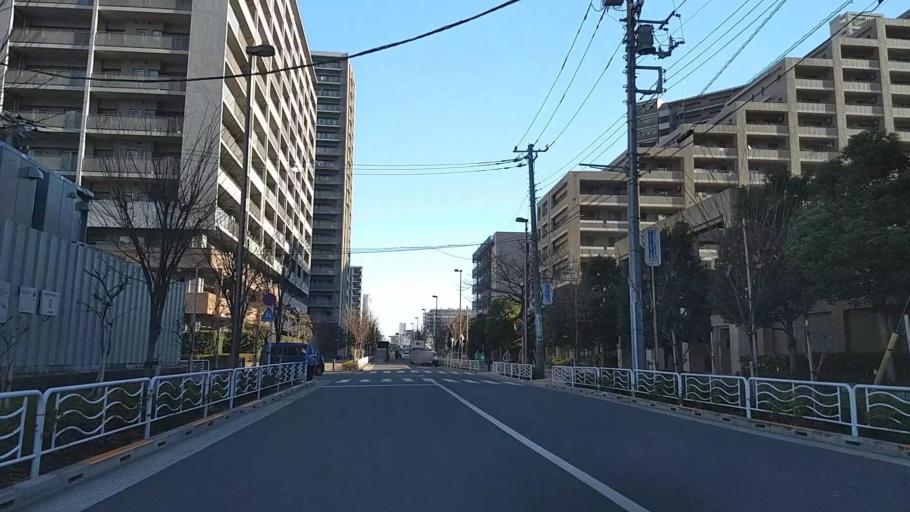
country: JP
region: Tokyo
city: Urayasu
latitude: 35.6544
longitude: 139.8005
